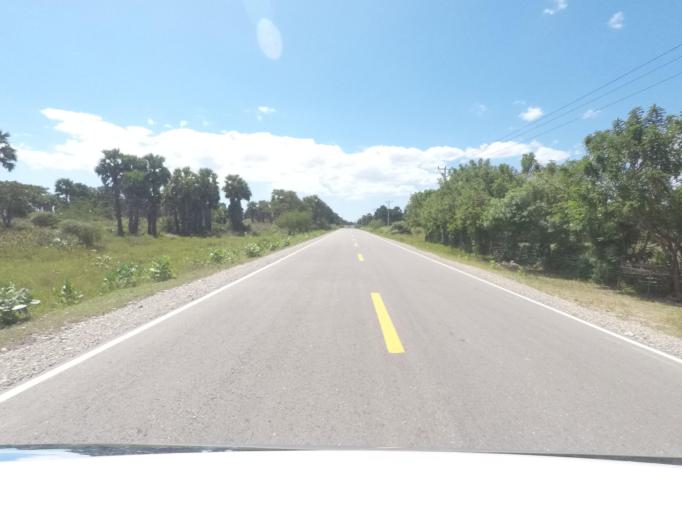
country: TL
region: Lautem
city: Lospalos
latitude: -8.3850
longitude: 126.8571
